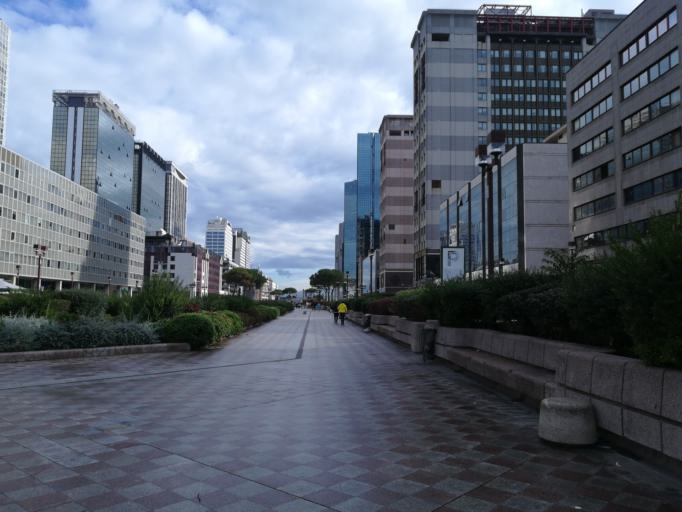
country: IT
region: Campania
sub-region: Provincia di Napoli
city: Napoli
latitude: 40.8564
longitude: 14.2775
